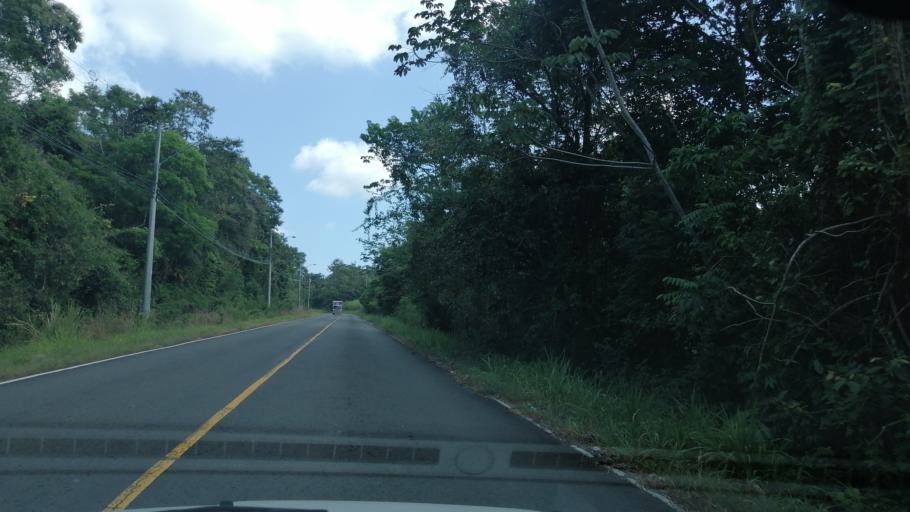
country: PA
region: Panama
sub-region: Distrito de Panama
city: Ancon
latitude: 8.9046
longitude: -79.5708
